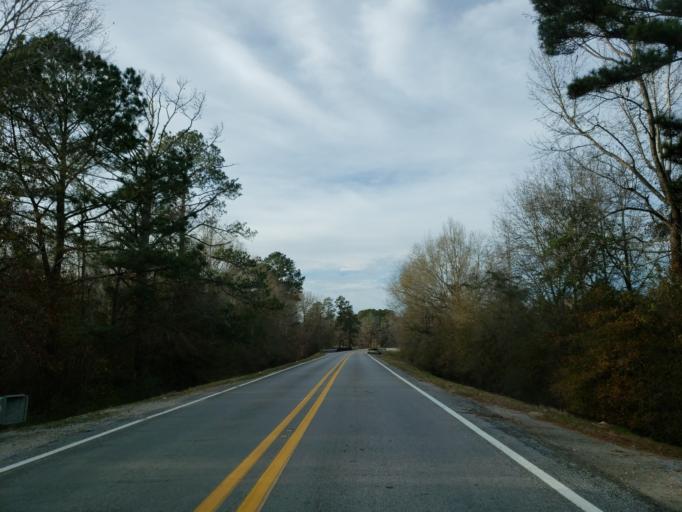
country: US
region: Mississippi
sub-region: Wayne County
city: Waynesboro
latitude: 31.8550
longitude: -88.6966
